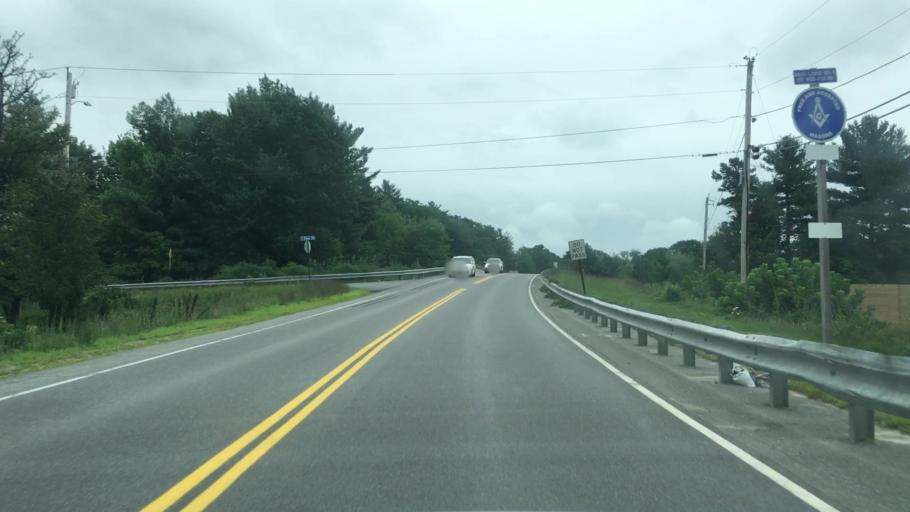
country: US
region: Maine
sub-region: York County
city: Biddeford
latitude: 43.5150
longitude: -70.4716
